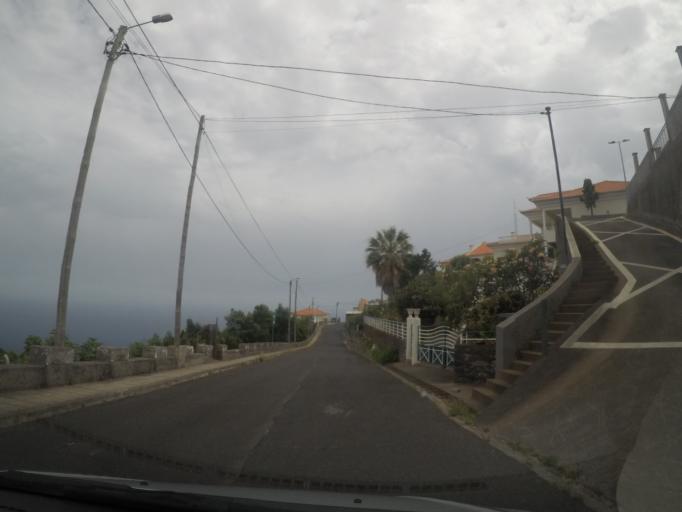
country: PT
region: Madeira
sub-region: Santa Cruz
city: Santa Cruz
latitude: 32.6807
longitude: -16.8092
